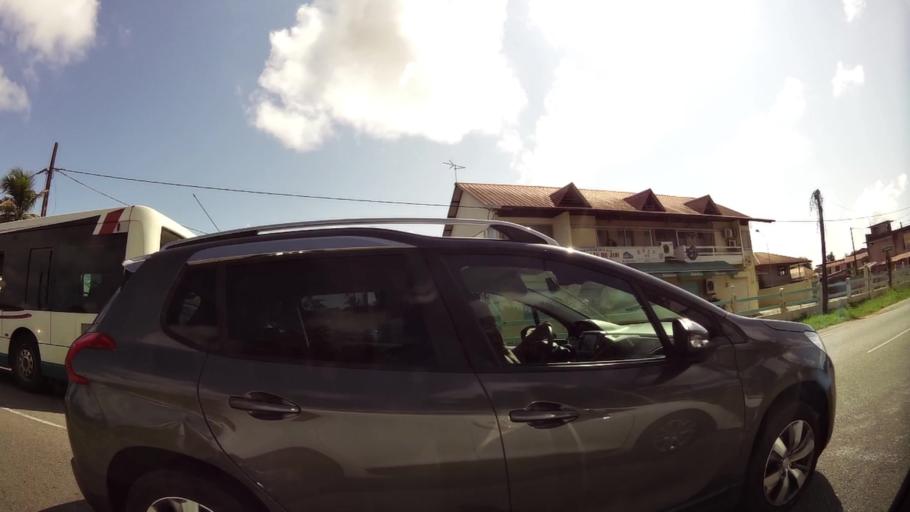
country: GF
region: Guyane
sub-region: Guyane
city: Cayenne
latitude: 4.9372
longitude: -52.3154
